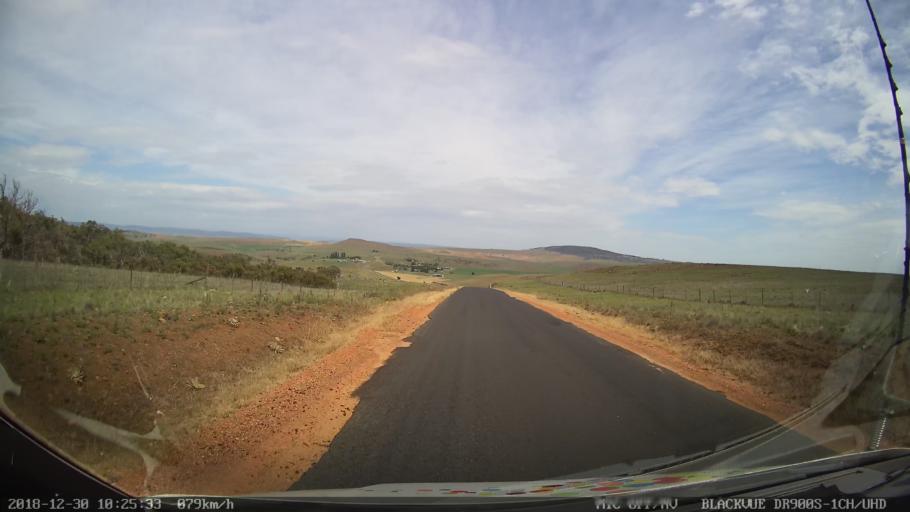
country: AU
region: New South Wales
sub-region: Snowy River
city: Berridale
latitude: -36.5234
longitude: 148.9579
